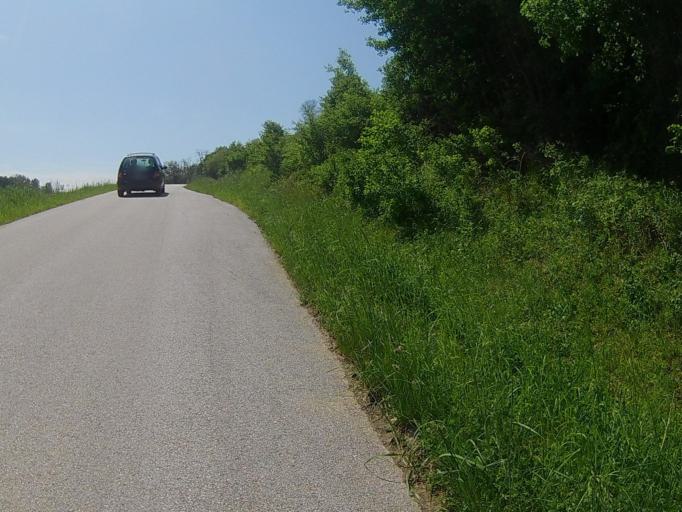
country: SI
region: Pesnica
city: Pesnica pri Mariboru
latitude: 46.5866
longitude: 15.6861
